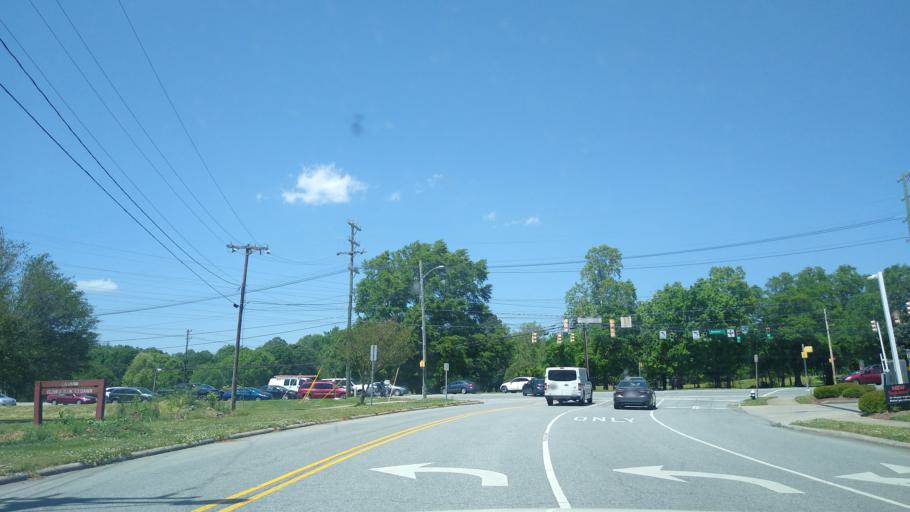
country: US
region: North Carolina
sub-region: Guilford County
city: Greensboro
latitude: 36.0876
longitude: -79.7945
